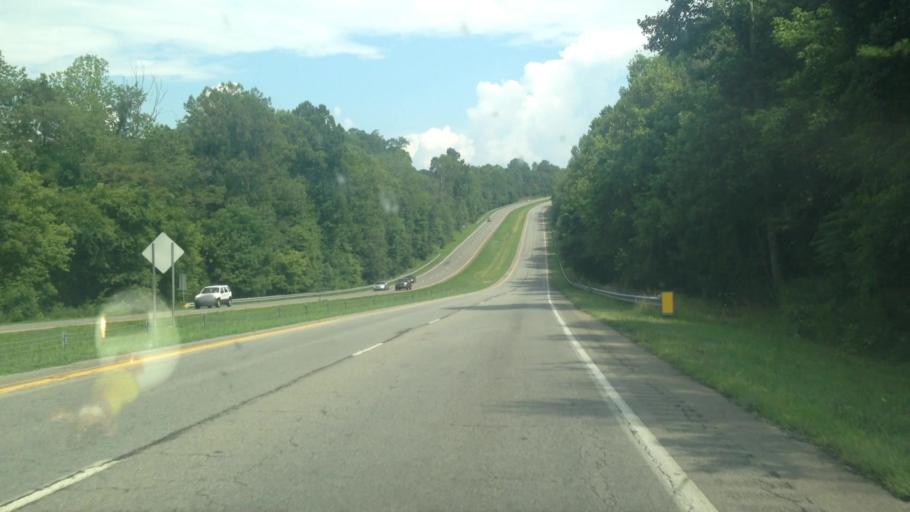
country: US
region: North Carolina
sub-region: Surry County
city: Flat Rock
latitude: 36.4678
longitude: -80.5702
